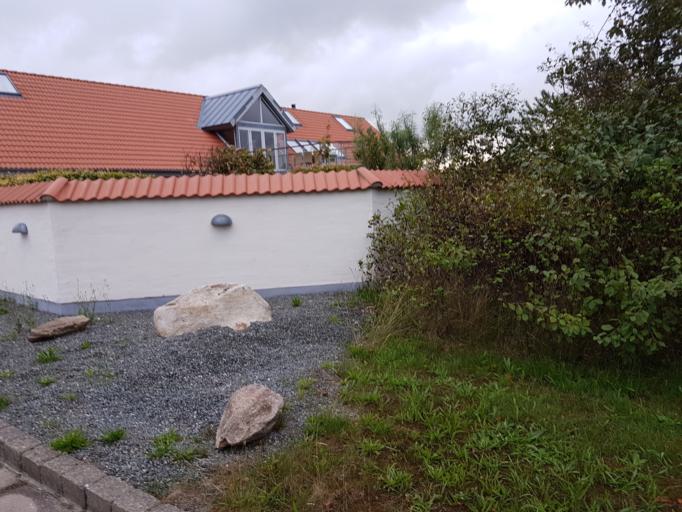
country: DK
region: Central Jutland
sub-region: Ringkobing-Skjern Kommune
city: Hvide Sande
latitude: 55.8518
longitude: 8.2917
